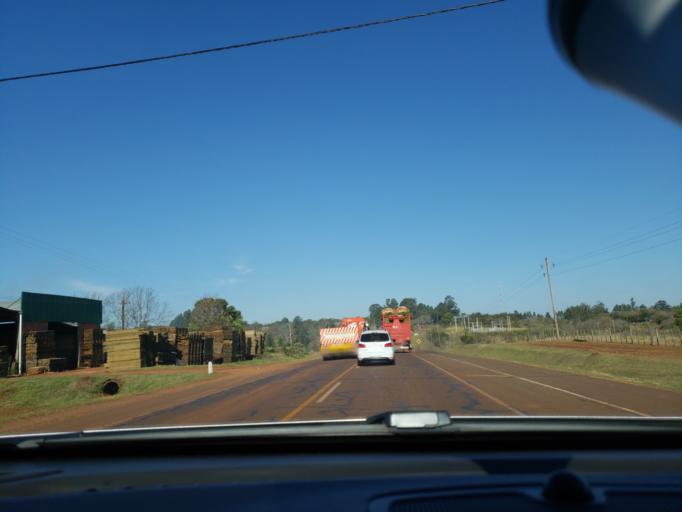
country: AR
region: Misiones
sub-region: Departamento de Apostoles
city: San Jose
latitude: -27.7586
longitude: -55.7738
